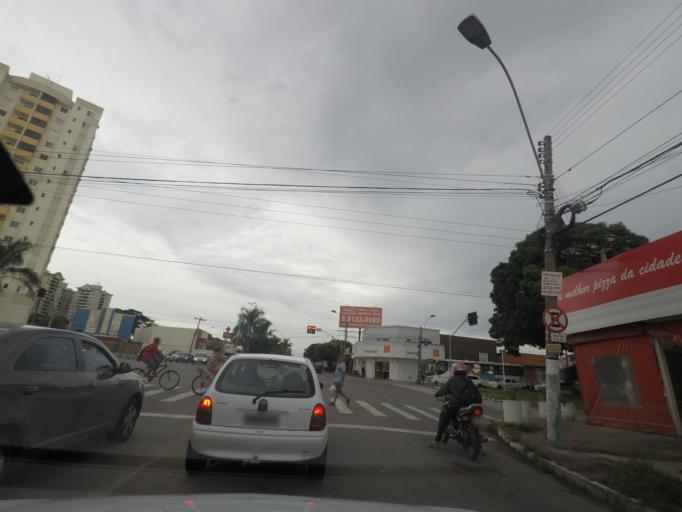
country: BR
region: Goias
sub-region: Goiania
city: Goiania
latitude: -16.7156
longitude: -49.2411
